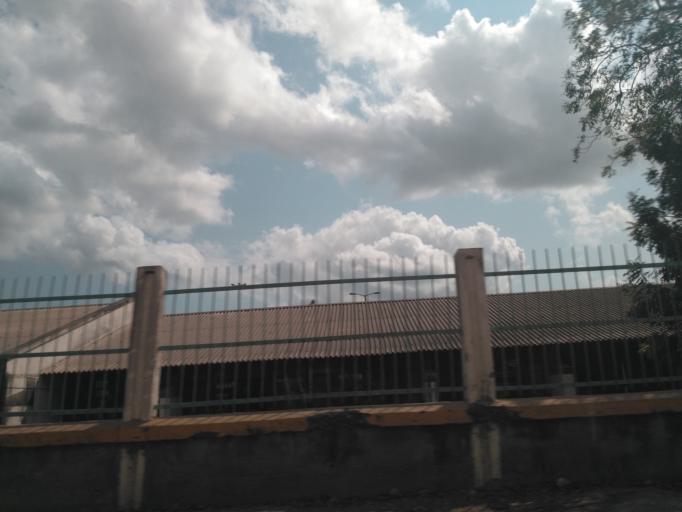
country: TZ
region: Dar es Salaam
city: Dar es Salaam
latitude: -6.8329
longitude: 39.2893
